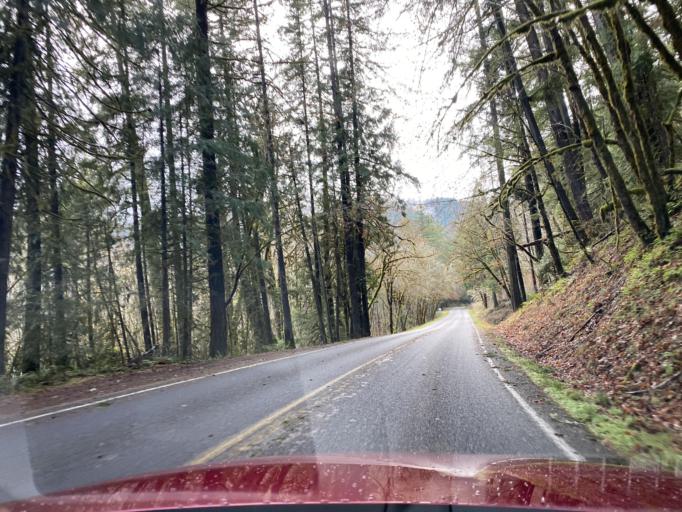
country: US
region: Oregon
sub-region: Lane County
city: Oakridge
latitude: 43.7478
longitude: -122.5153
